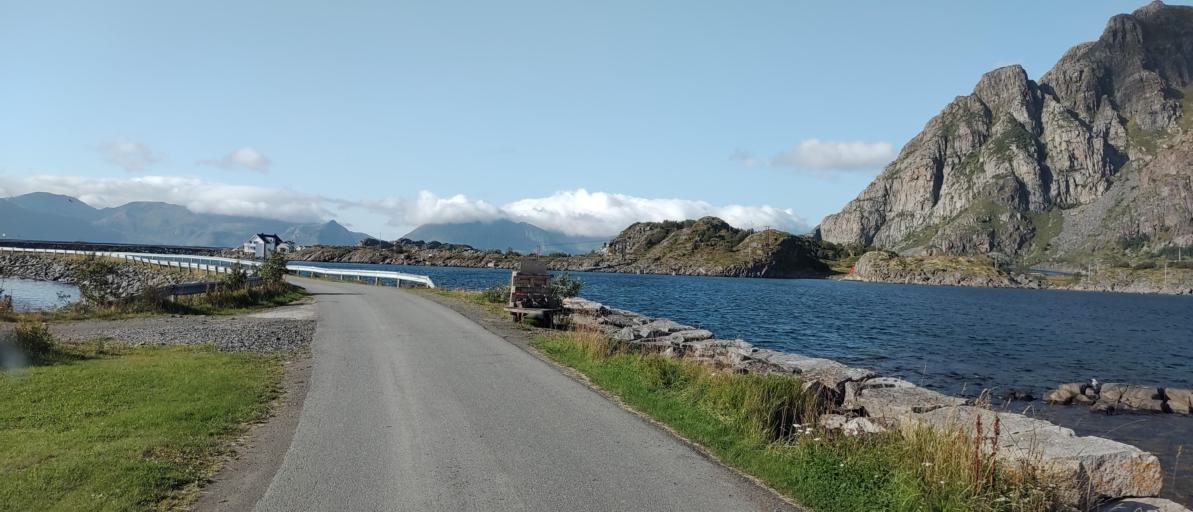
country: NO
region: Nordland
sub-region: Vagan
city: Kabelvag
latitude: 68.1603
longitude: 14.2224
